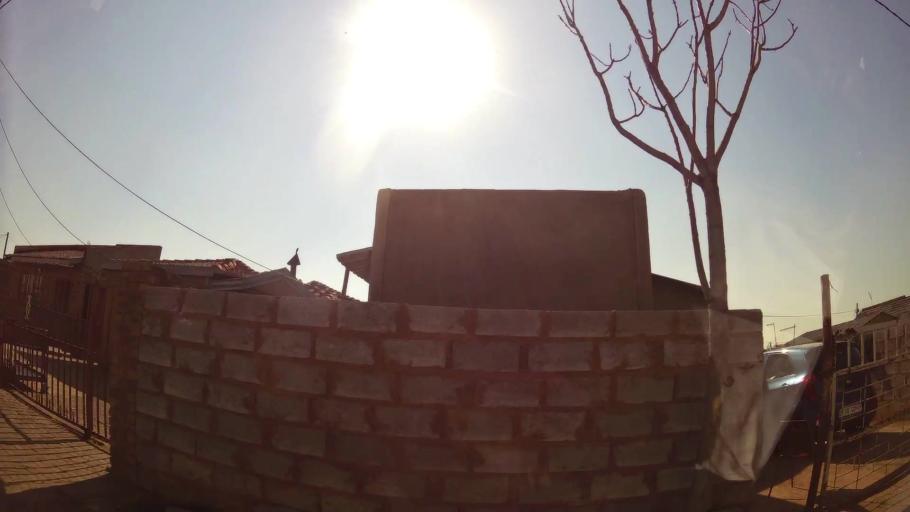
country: ZA
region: Gauteng
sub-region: Ekurhuleni Metropolitan Municipality
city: Boksburg
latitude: -26.2299
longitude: 28.2991
